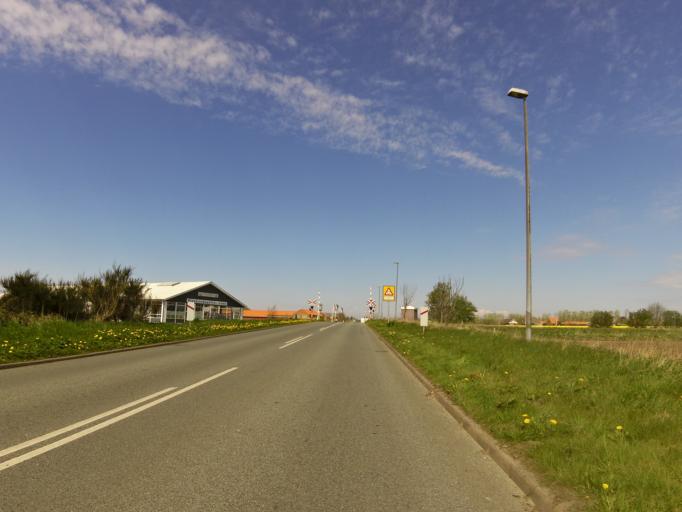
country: DK
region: South Denmark
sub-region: Tonder Kommune
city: Sherrebek
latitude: 55.1515
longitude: 8.7821
